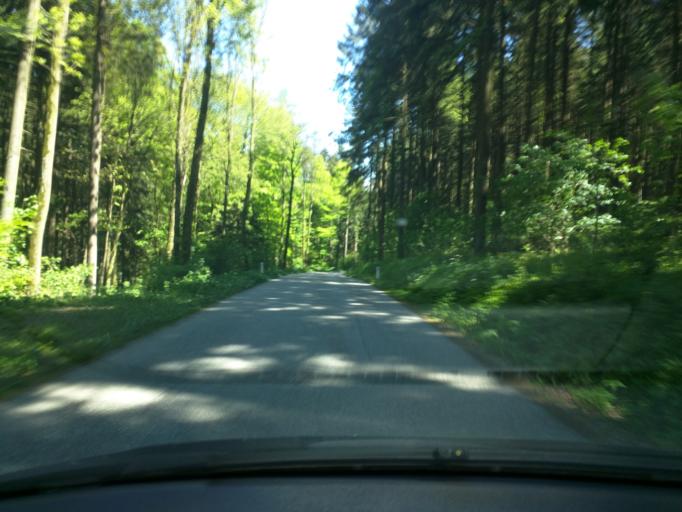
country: AT
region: Lower Austria
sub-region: Politischer Bezirk Melk
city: Blindenmarkt
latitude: 48.1591
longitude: 14.9725
